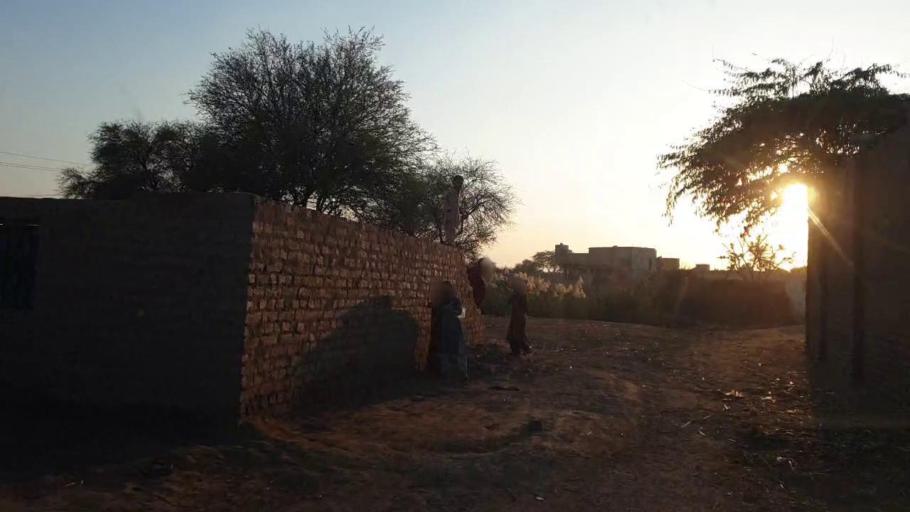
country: PK
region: Sindh
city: Chambar
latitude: 25.3675
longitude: 68.7473
